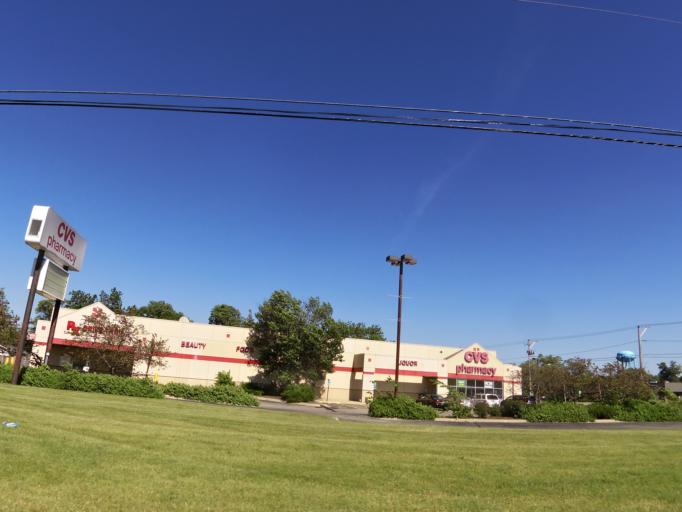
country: US
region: Illinois
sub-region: Winnebago County
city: Machesney Park
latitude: 42.3402
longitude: -89.0526
